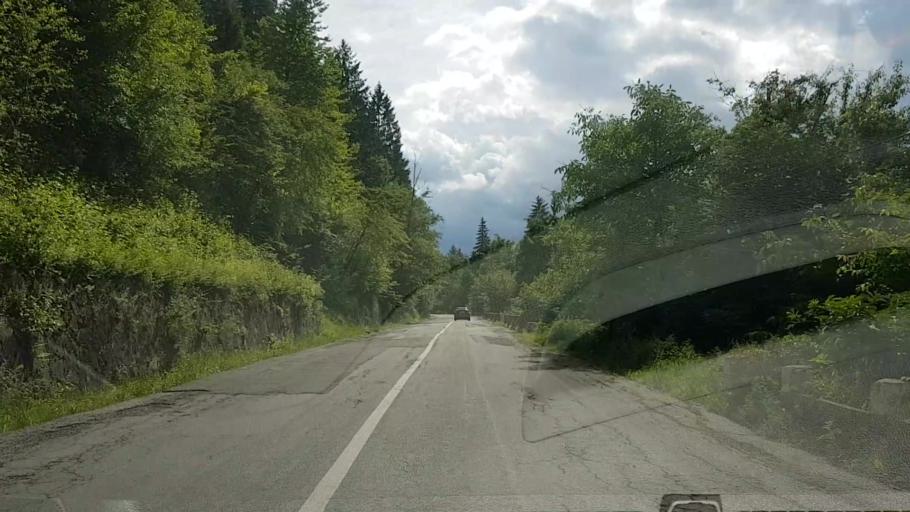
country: RO
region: Neamt
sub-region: Comuna Hangu
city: Hangu
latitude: 47.0168
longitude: 26.0866
